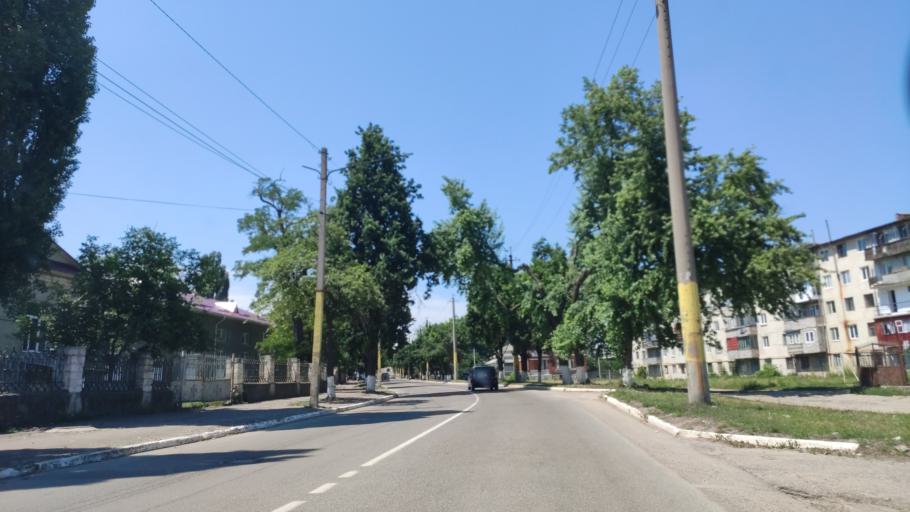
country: MD
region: Raionul Soroca
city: Soroca
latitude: 48.1616
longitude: 28.2903
